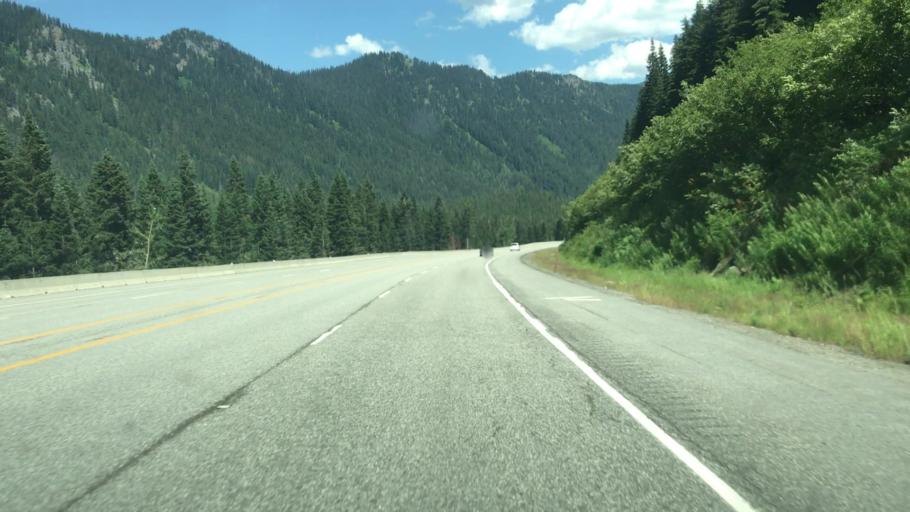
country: US
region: Washington
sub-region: Chelan County
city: Leavenworth
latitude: 47.7800
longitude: -121.0615
